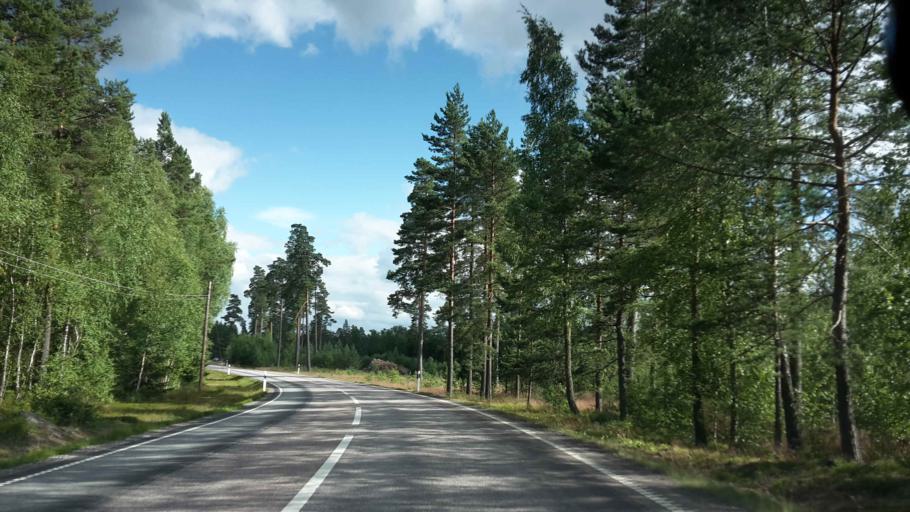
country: SE
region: OErebro
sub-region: Hallsbergs Kommun
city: Palsboda
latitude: 58.8378
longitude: 15.4047
